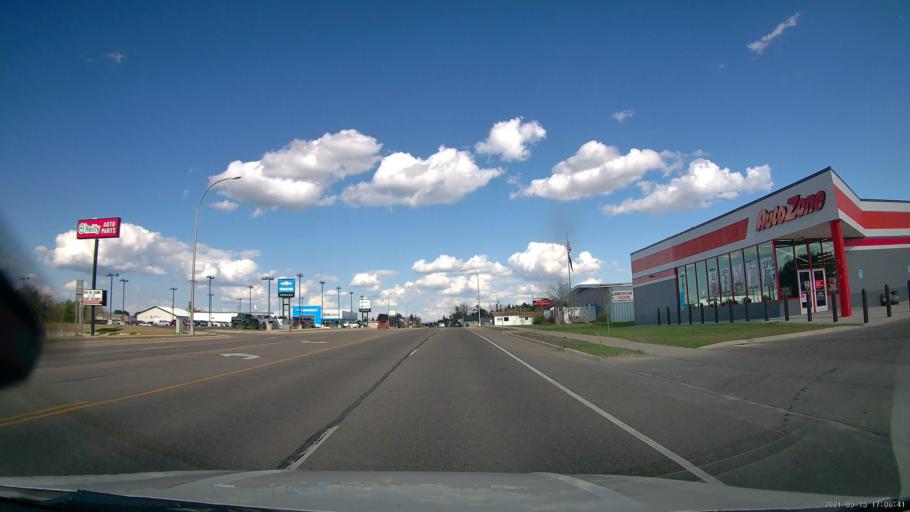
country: US
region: Minnesota
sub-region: Hubbard County
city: Park Rapids
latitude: 46.9220
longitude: -95.0454
